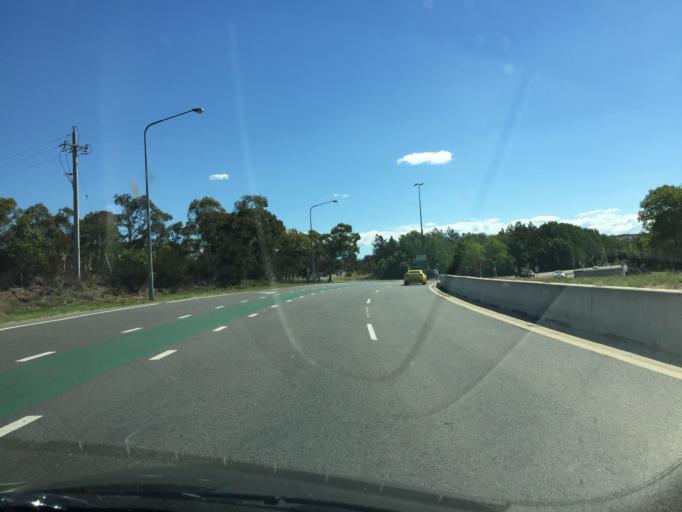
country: AU
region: Australian Capital Territory
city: Macarthur
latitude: -35.3836
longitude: 149.1733
